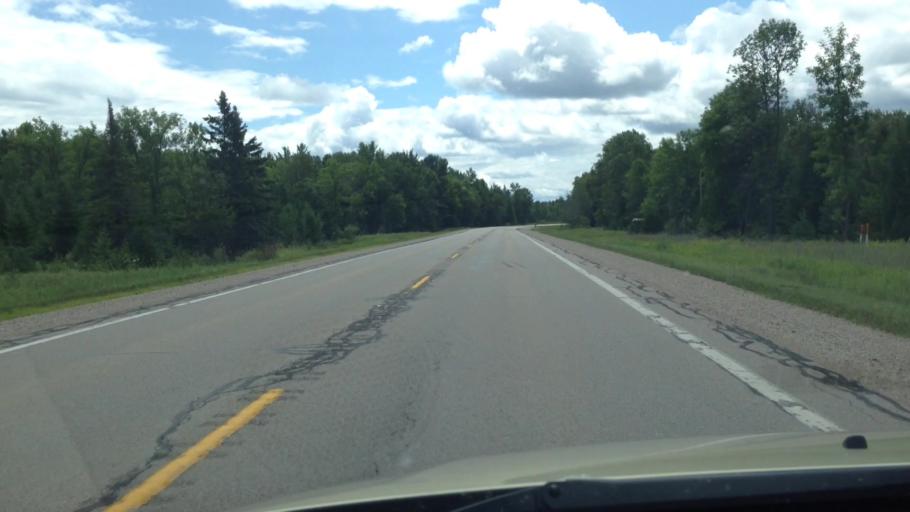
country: US
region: Michigan
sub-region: Menominee County
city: Menominee
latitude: 45.3604
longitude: -87.3989
